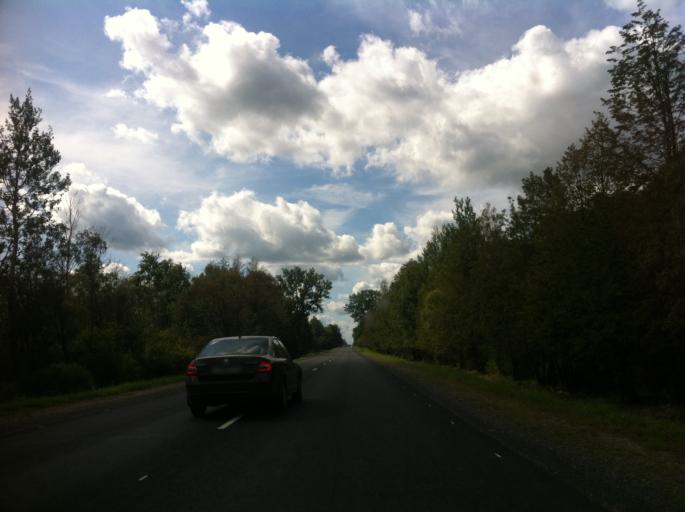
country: RU
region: Pskov
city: Izborsk
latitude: 57.7603
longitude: 28.0870
